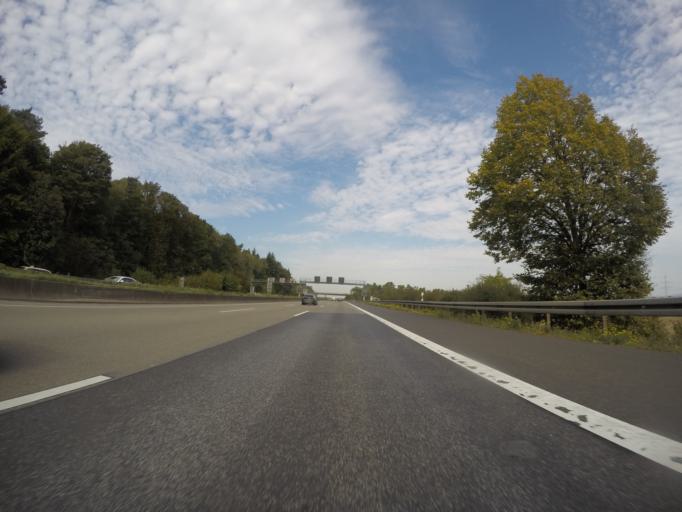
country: DE
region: Hesse
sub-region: Regierungsbezirk Darmstadt
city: Seligenstadt
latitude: 50.0373
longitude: 8.9362
